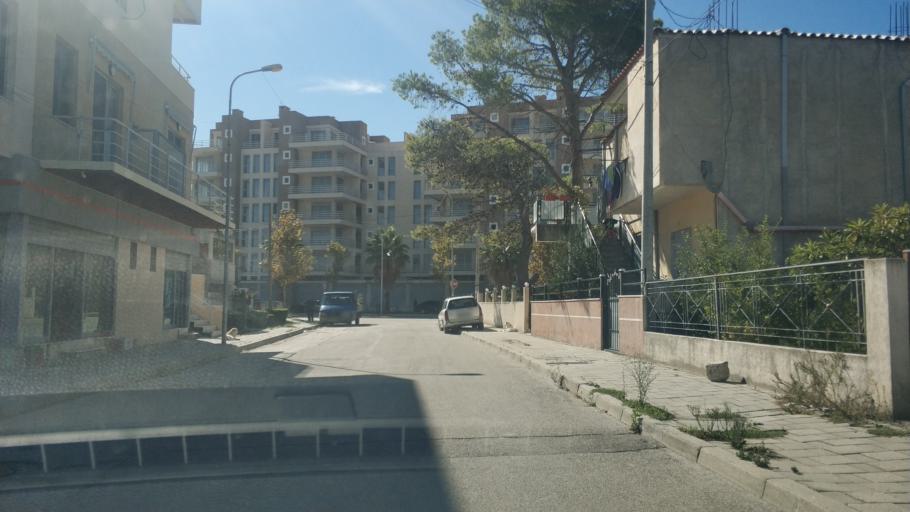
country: AL
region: Vlore
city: Vlore
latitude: 40.4586
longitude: 19.4689
